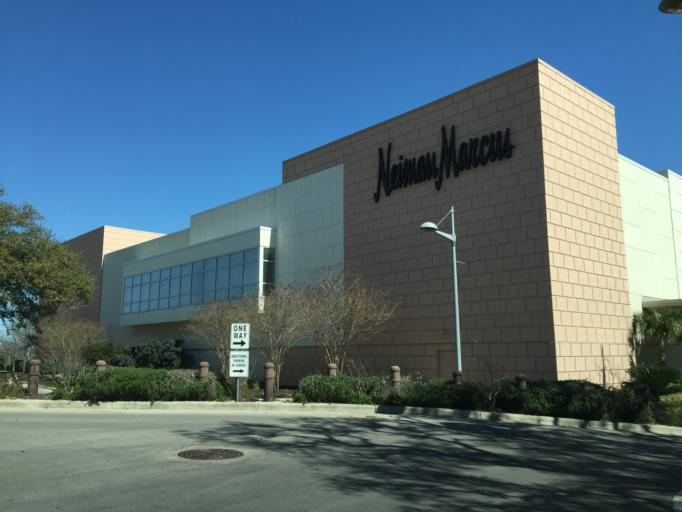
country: US
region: Texas
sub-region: Travis County
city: Wells Branch
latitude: 30.4039
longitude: -97.7251
